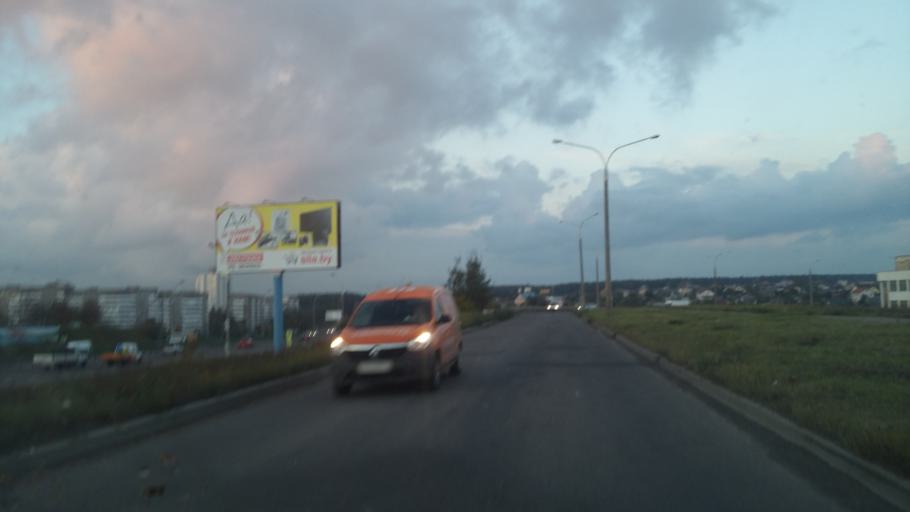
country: BY
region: Minsk
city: Vyaliki Trastsyanets
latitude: 53.8657
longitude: 27.6889
